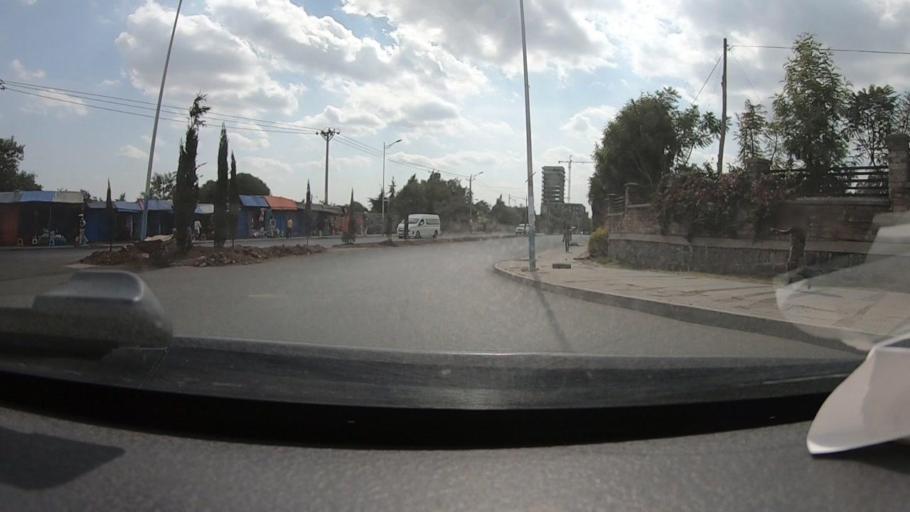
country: ET
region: Adis Abeba
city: Addis Ababa
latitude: 9.0466
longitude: 38.7679
